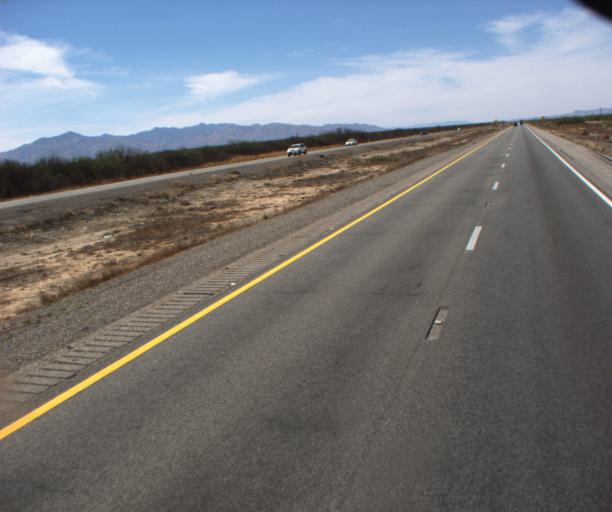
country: US
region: Arizona
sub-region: Cochise County
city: Willcox
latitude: 32.2863
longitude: -109.3052
